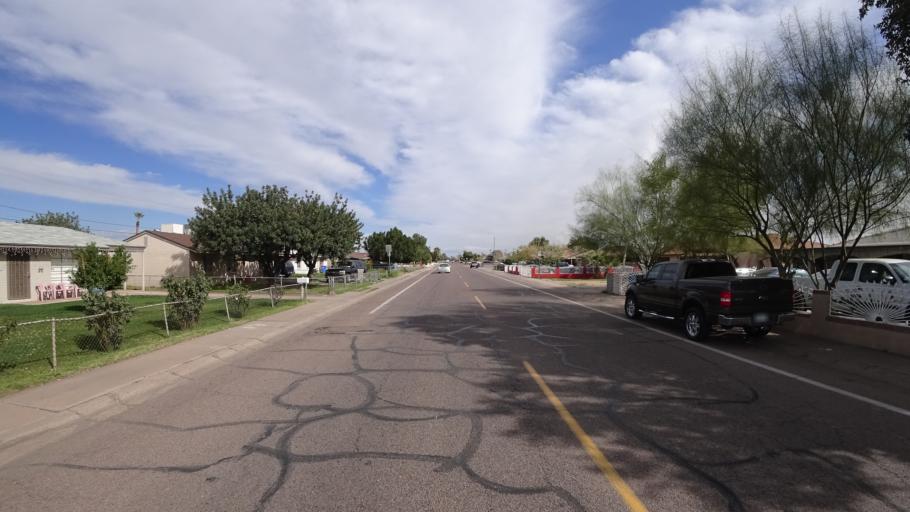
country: US
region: Arizona
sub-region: Maricopa County
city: Phoenix
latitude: 33.4730
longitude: -112.1400
